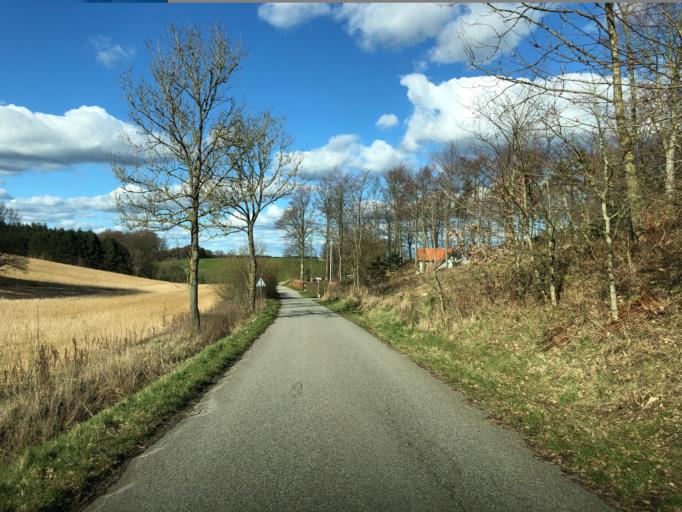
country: DK
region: Central Jutland
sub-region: Favrskov Kommune
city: Hammel
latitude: 56.3037
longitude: 9.9179
